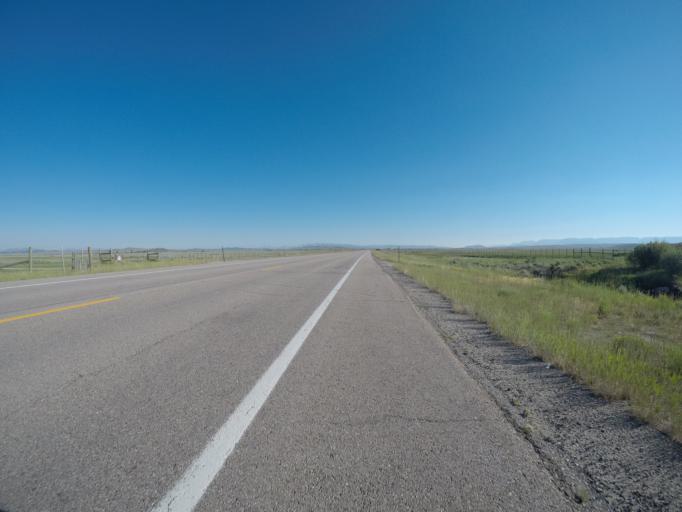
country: US
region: Wyoming
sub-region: Sublette County
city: Pinedale
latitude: 42.9528
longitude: -110.0864
